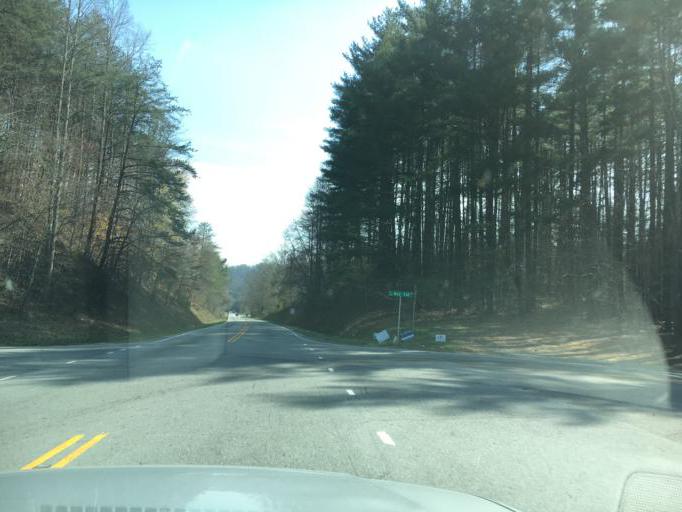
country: US
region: North Carolina
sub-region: McDowell County
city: West Marion
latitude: 35.5868
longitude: -81.9827
